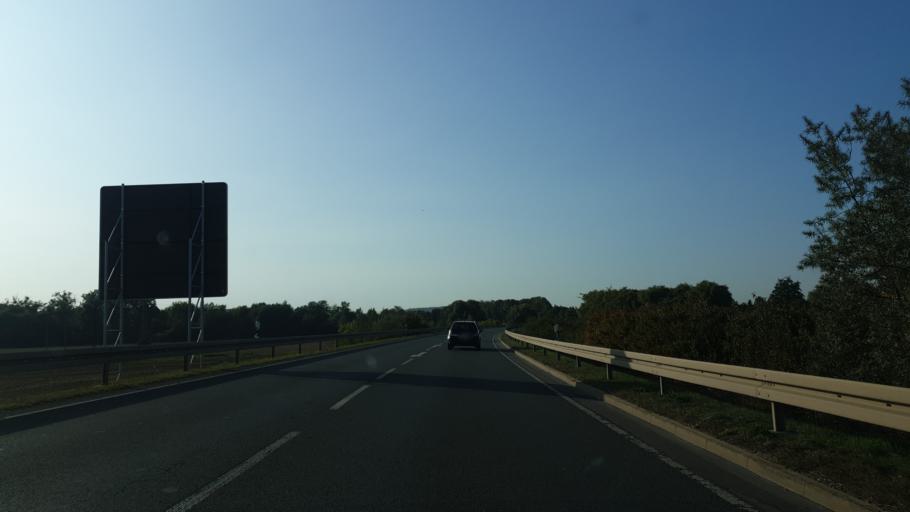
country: DE
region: Thuringia
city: Bad Kostritz
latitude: 50.9268
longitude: 12.0317
